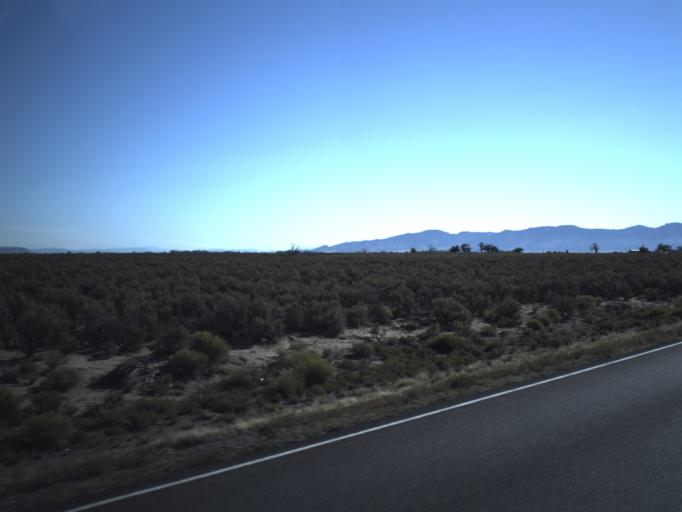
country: US
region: Utah
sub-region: Washington County
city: Enterprise
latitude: 37.7277
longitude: -113.7071
